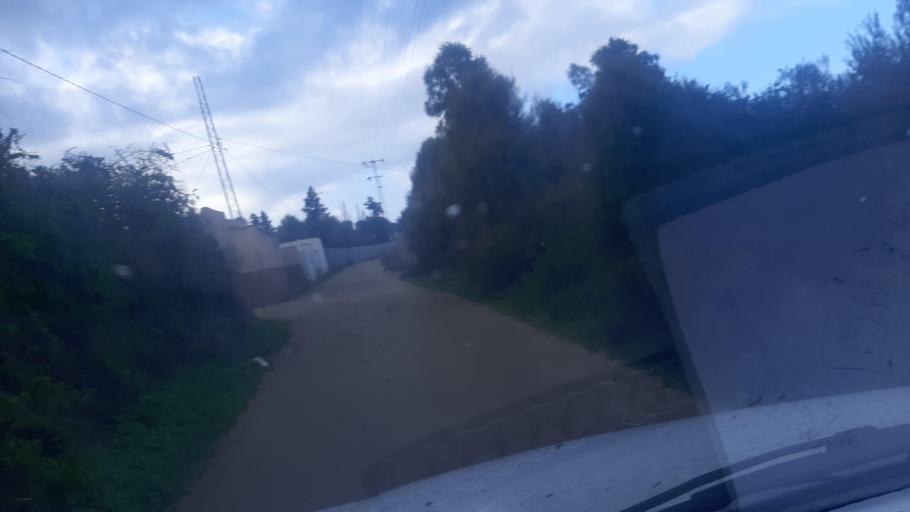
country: TN
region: Nabul
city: Manzil Bu Zalafah
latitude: 36.7417
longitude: 10.5282
